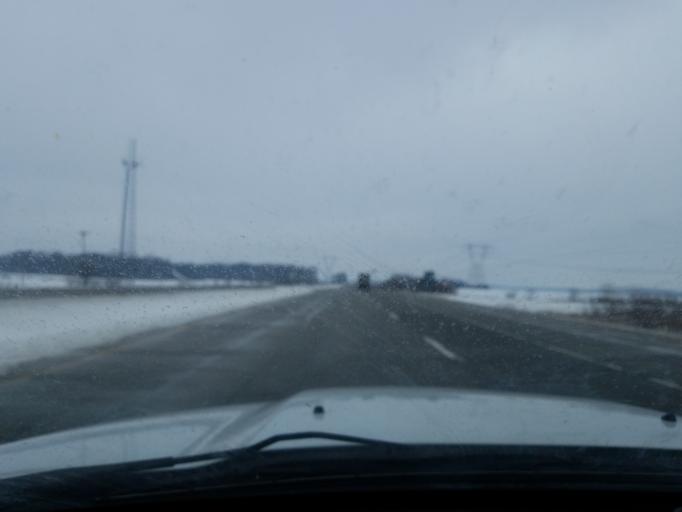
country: US
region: Indiana
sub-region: Marshall County
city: Argos
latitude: 41.2004
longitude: -86.2563
